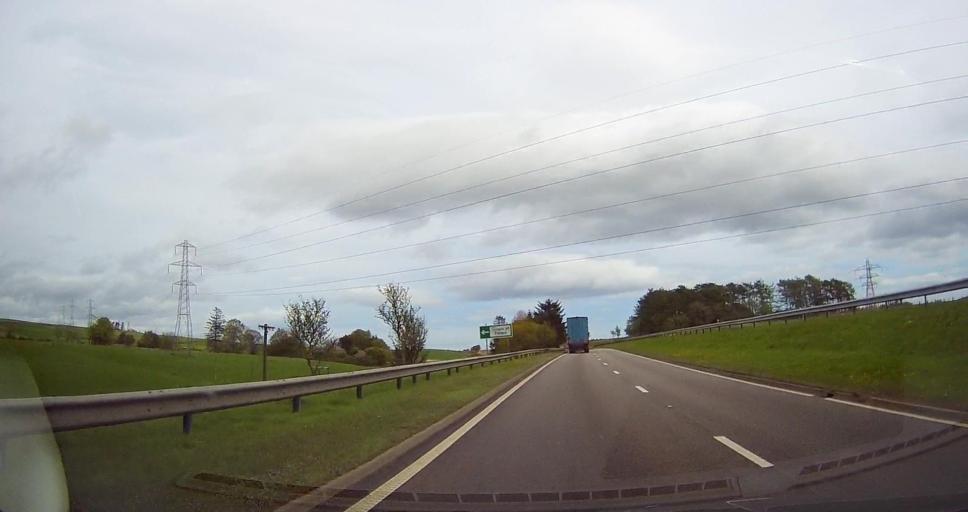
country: GB
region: Scotland
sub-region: Aberdeenshire
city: Inverbervie
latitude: 56.9248
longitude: -2.3071
